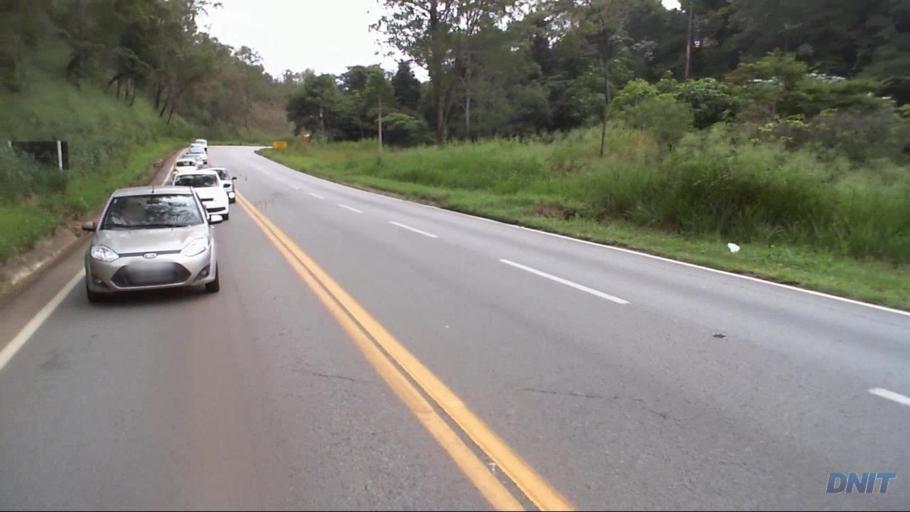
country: BR
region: Minas Gerais
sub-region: Nova Era
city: Nova Era
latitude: -19.8225
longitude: -43.0765
